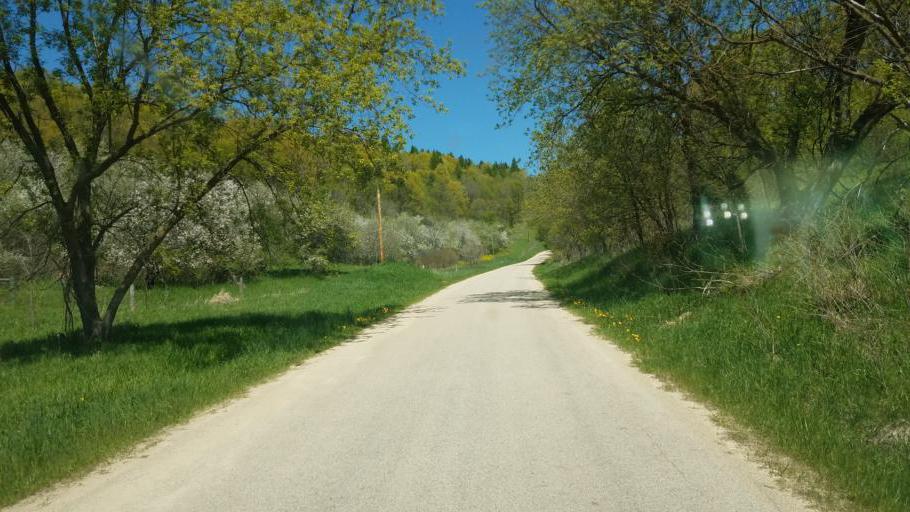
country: US
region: Wisconsin
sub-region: Vernon County
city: Hillsboro
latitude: 43.6259
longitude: -90.4825
